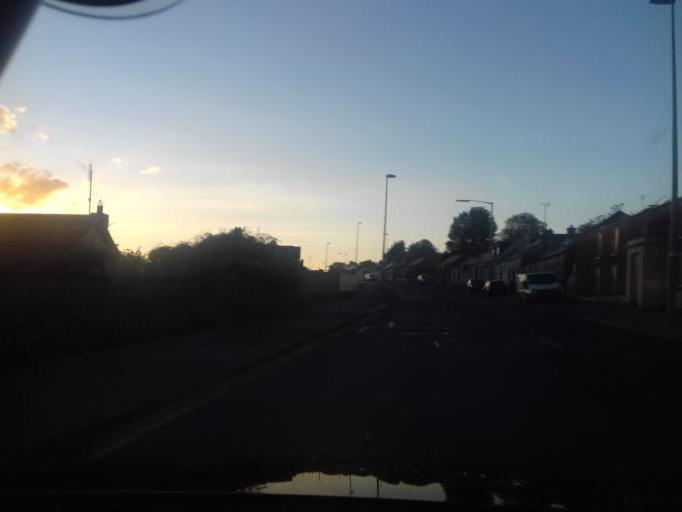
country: IE
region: Leinster
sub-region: Lu
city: Drogheda
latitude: 53.7184
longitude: -6.3647
